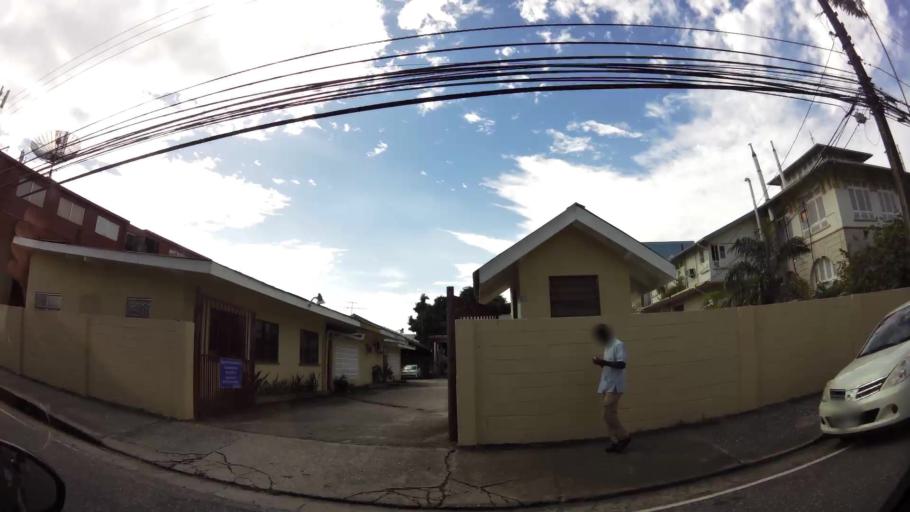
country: TT
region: City of Port of Spain
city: Port-of-Spain
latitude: 10.6620
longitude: -61.5100
